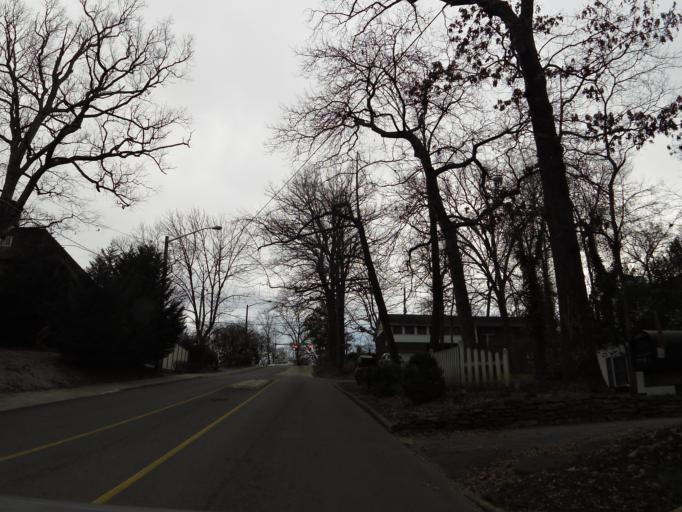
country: US
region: Tennessee
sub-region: Knox County
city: Knoxville
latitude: 35.9447
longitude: -83.9711
